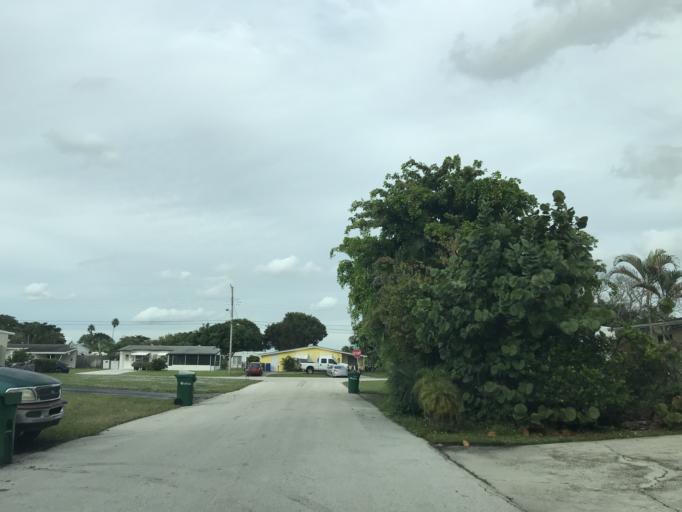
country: US
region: Florida
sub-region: Broward County
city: Margate
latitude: 26.2598
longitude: -80.2055
